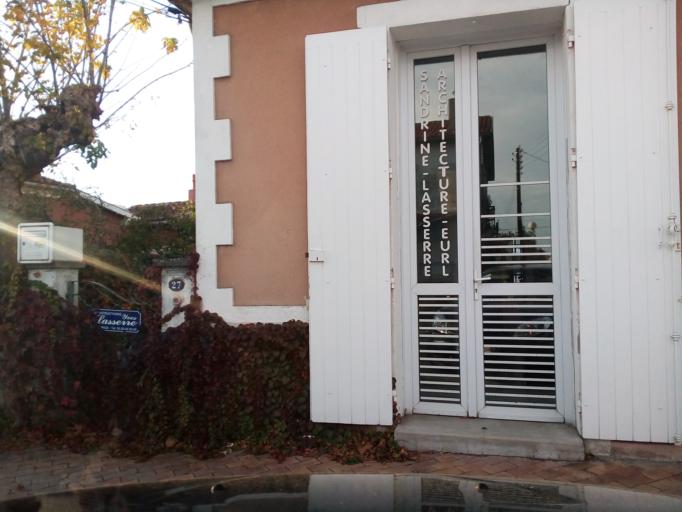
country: FR
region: Aquitaine
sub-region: Departement de la Gironde
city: Andernos-les-Bains
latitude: 44.7439
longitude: -1.0959
